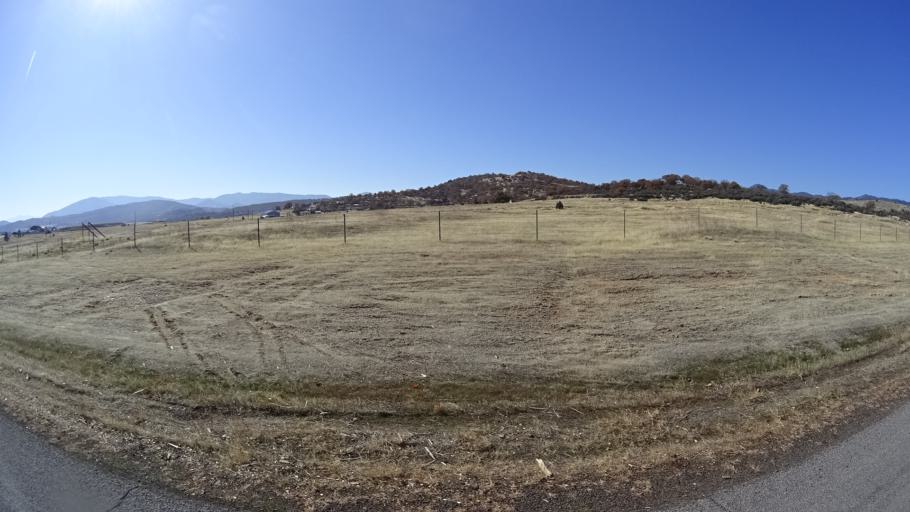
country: US
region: California
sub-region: Siskiyou County
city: Yreka
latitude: 41.7404
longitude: -122.5982
